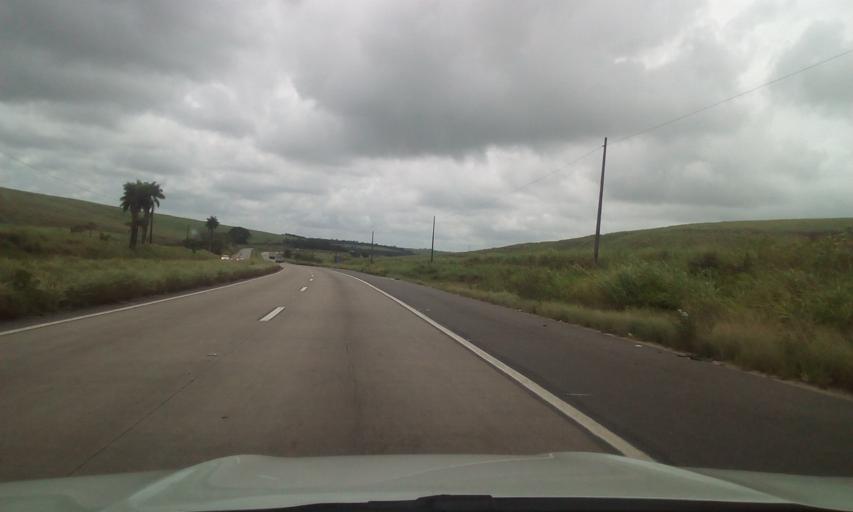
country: BR
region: Pernambuco
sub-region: Itapissuma
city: Itapissuma
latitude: -7.7806
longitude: -34.9317
